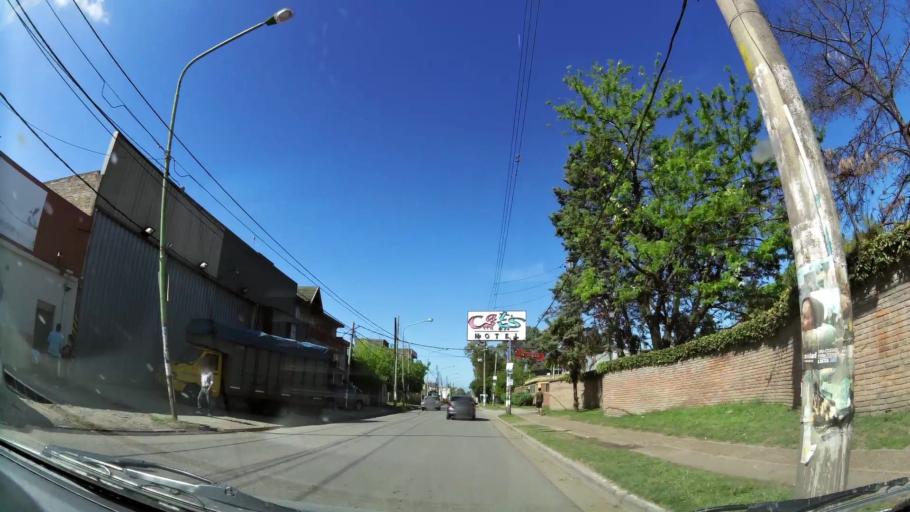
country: AR
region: Buenos Aires
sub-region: Partido de Quilmes
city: Quilmes
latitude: -34.8043
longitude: -58.2460
